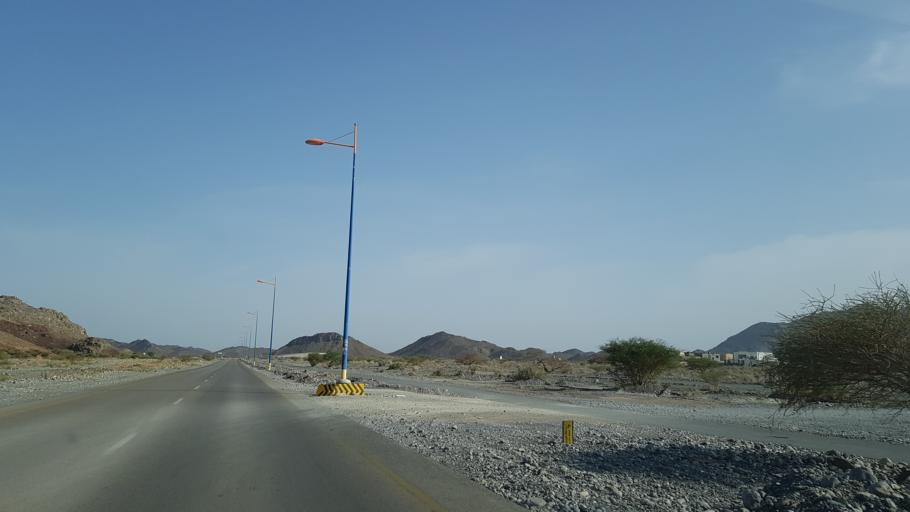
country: OM
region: Muhafazat ad Dakhiliyah
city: Izki
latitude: 22.9021
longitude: 57.6793
